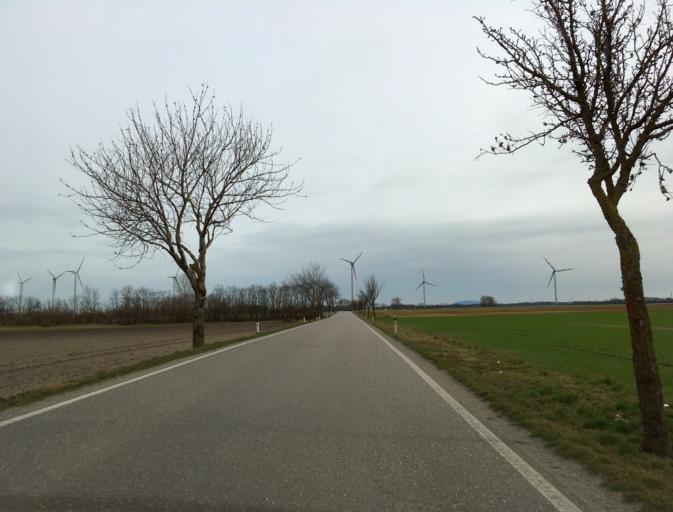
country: AT
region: Lower Austria
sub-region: Politischer Bezirk Ganserndorf
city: Glinzendorf
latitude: 48.2469
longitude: 16.6503
